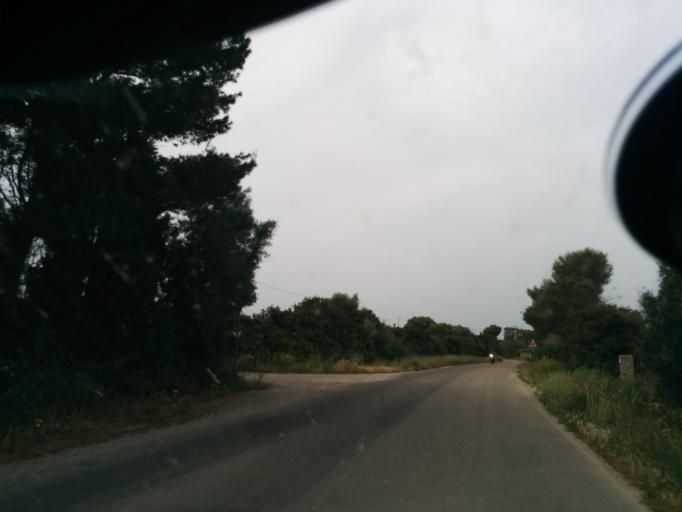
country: IT
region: Sardinia
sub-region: Provincia di Carbonia-Iglesias
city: Sant'Antioco
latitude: 39.0309
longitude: 8.4520
